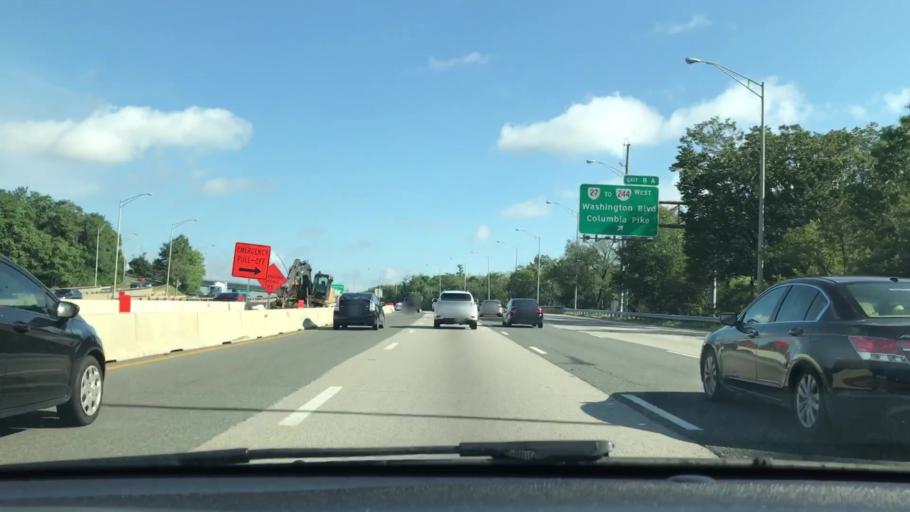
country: US
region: Virginia
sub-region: Arlington County
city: Arlington
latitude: 38.8584
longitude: -77.0701
